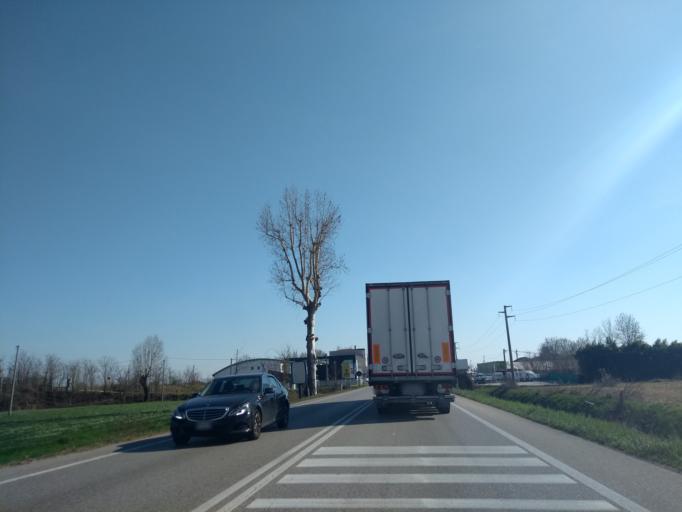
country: IT
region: Veneto
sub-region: Provincia di Padova
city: Curtarolo
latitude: 45.4967
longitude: 11.8304
